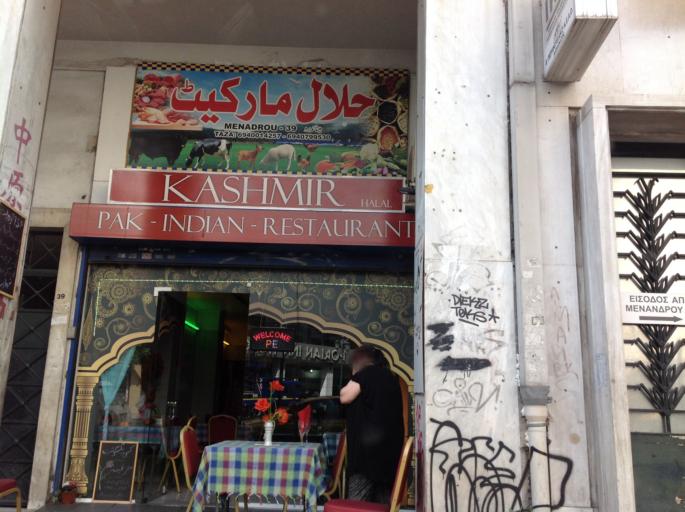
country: GR
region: Attica
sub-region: Nomarchia Athinas
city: Athens
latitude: 37.9830
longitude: 23.7251
